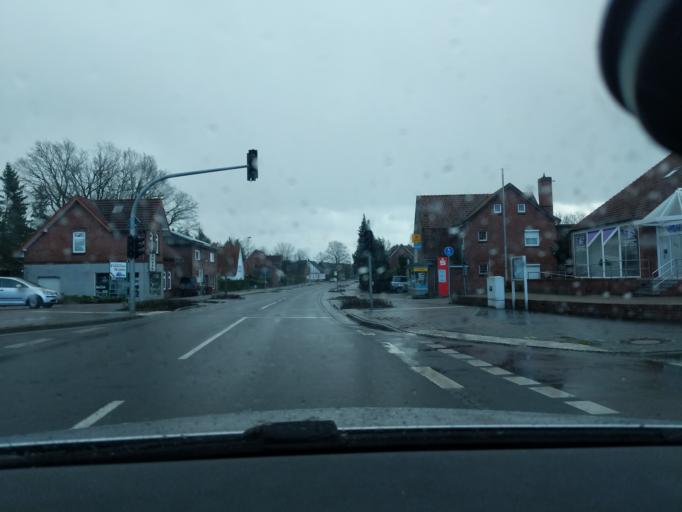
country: DE
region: Lower Saxony
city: Hemmoor
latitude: 53.6867
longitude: 9.1731
